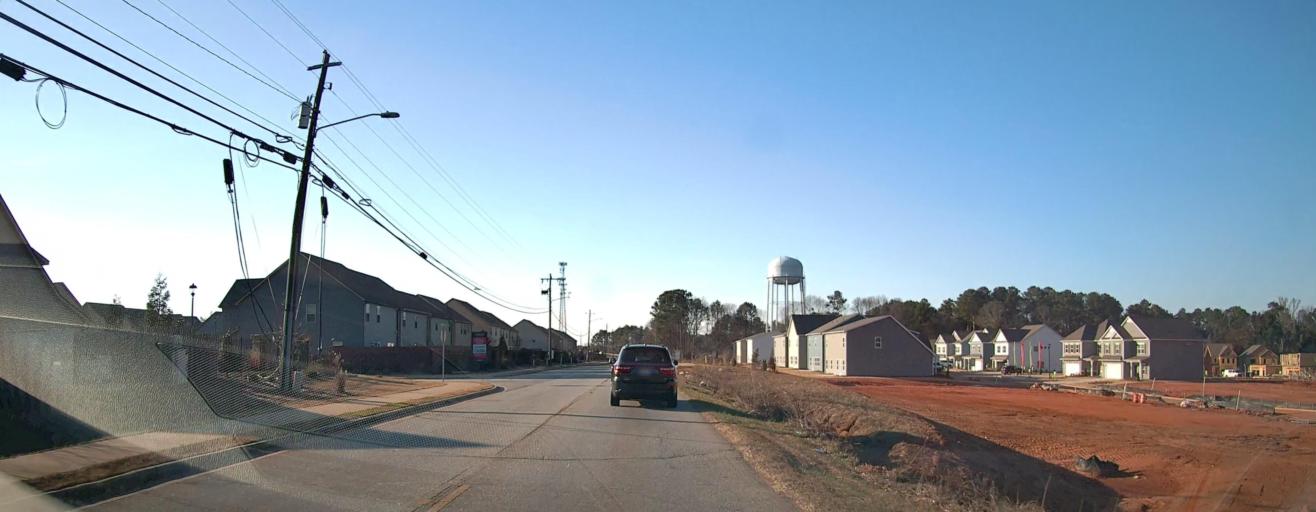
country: US
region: Georgia
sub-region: Clayton County
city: Lovejoy
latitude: 33.4466
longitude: -84.3184
